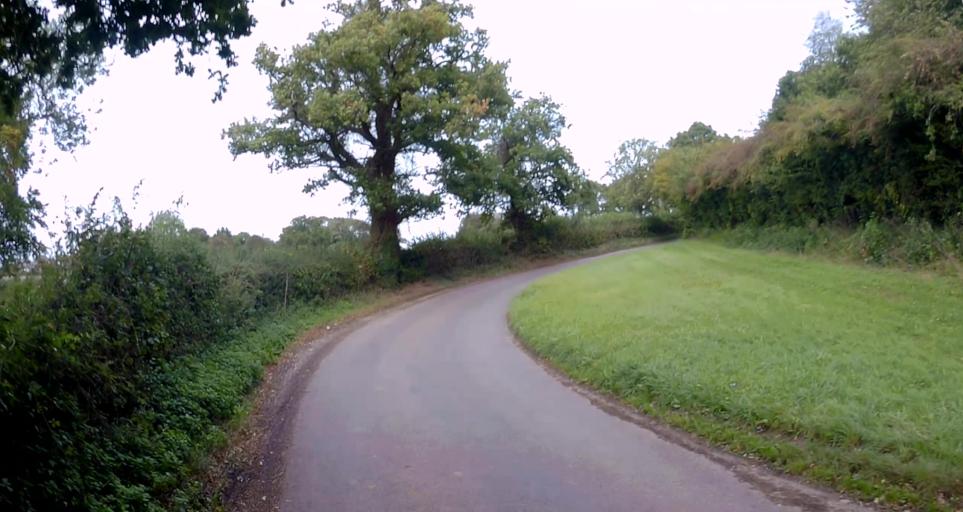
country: GB
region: England
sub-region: Hampshire
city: Four Marks
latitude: 51.1139
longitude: -1.1037
